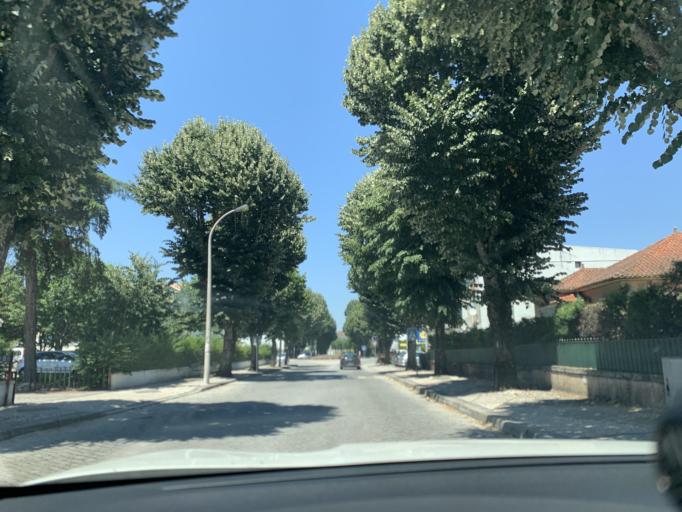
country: PT
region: Viseu
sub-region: Nelas
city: Nelas
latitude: 40.5326
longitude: -7.8541
